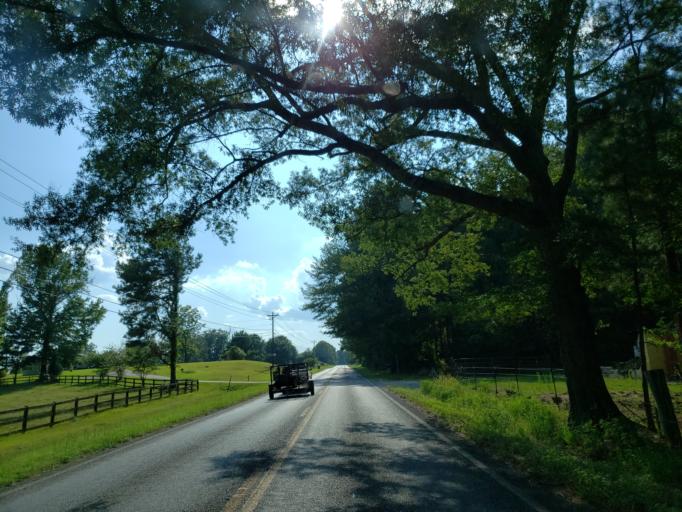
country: US
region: Mississippi
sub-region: Jones County
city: Sharon
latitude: 31.9197
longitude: -89.0317
